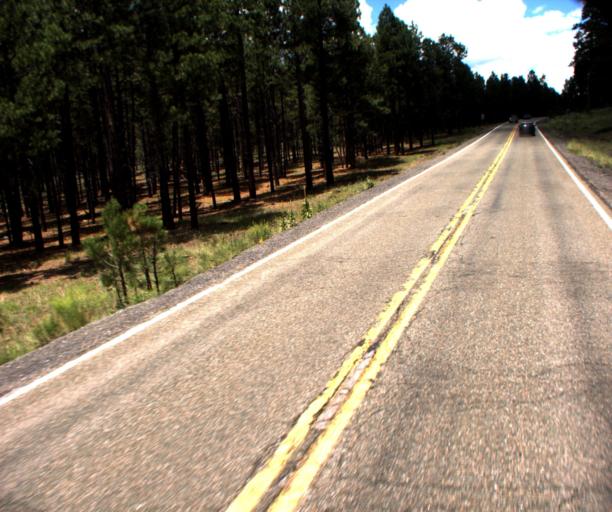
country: US
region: Arizona
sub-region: Coconino County
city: Parks
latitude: 35.3508
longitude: -111.7906
